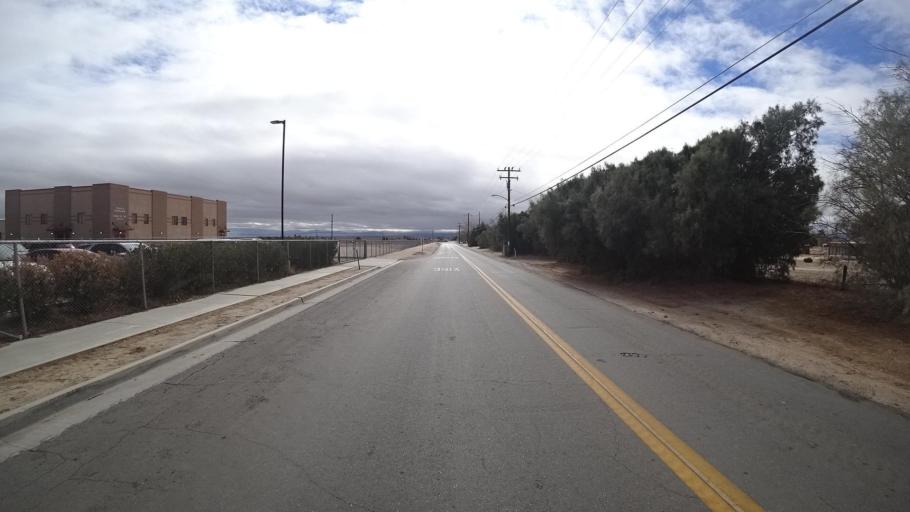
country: US
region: California
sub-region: Kern County
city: Rosamond
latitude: 34.8659
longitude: -118.2291
